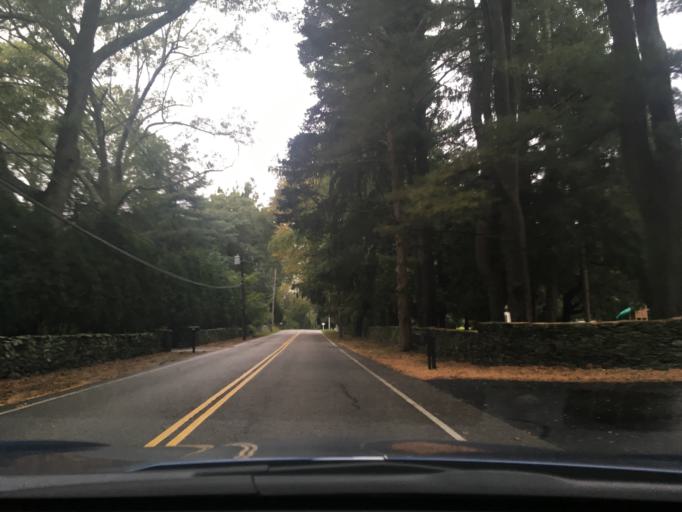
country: US
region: Rhode Island
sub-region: Kent County
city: East Greenwich
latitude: 41.6403
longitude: -71.4383
